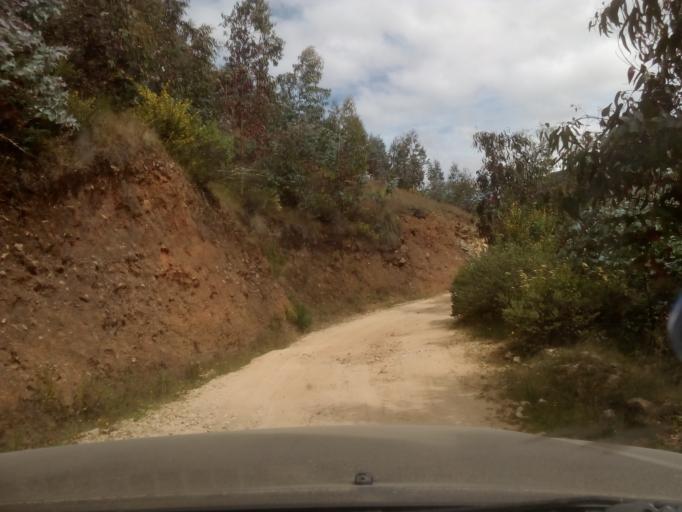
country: PE
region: La Libertad
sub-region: Sanchez Carrion
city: Curgos
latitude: -7.8731
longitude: -77.9618
